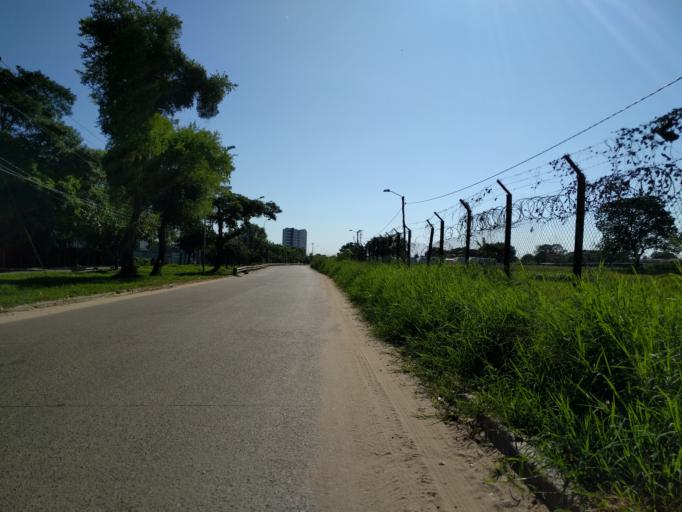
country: BO
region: Santa Cruz
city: Santa Cruz de la Sierra
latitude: -17.8017
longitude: -63.2259
